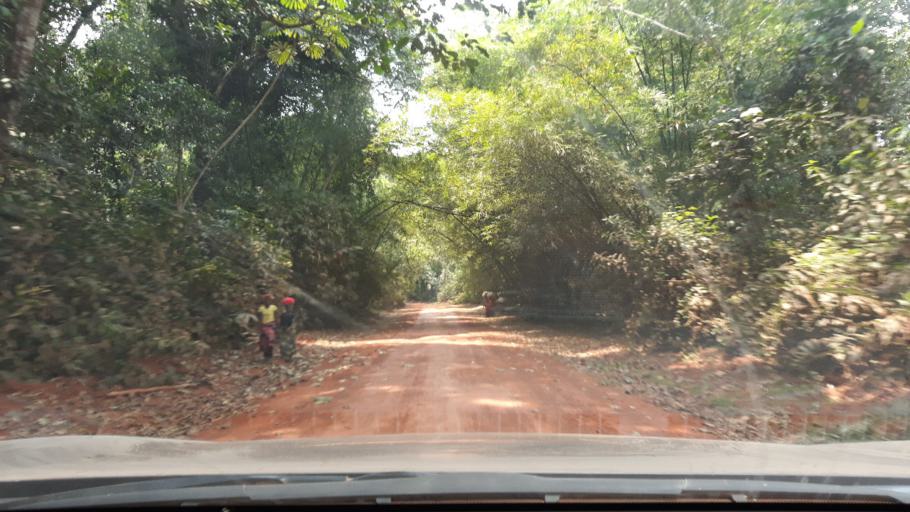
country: CD
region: Eastern Province
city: Buta
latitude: 2.2829
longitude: 25.1195
